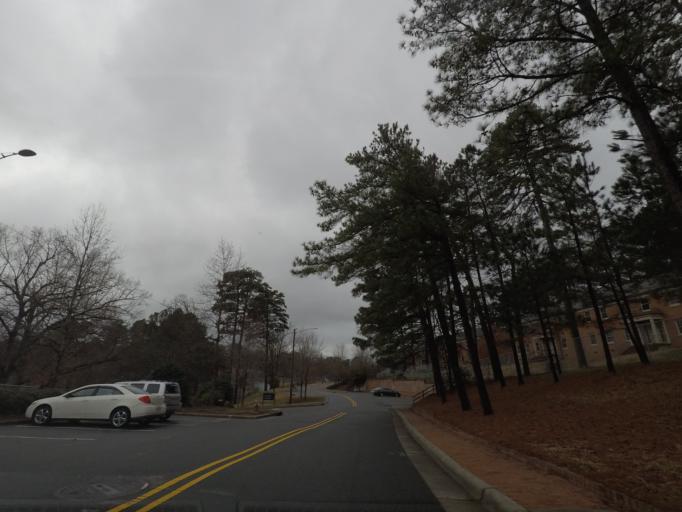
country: US
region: North Carolina
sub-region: Orange County
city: Chapel Hill
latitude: 35.9009
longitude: -79.0496
